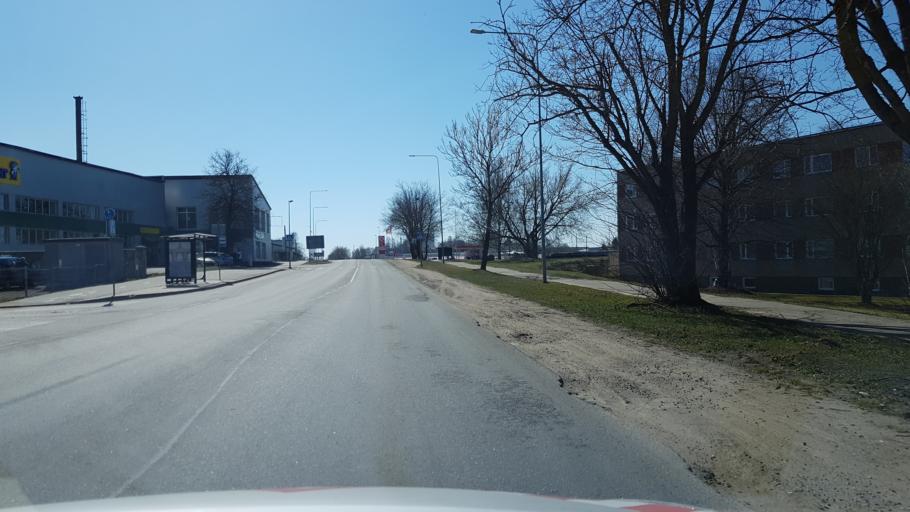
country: EE
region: Ida-Virumaa
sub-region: Johvi vald
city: Johvi
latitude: 59.3530
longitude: 27.4102
